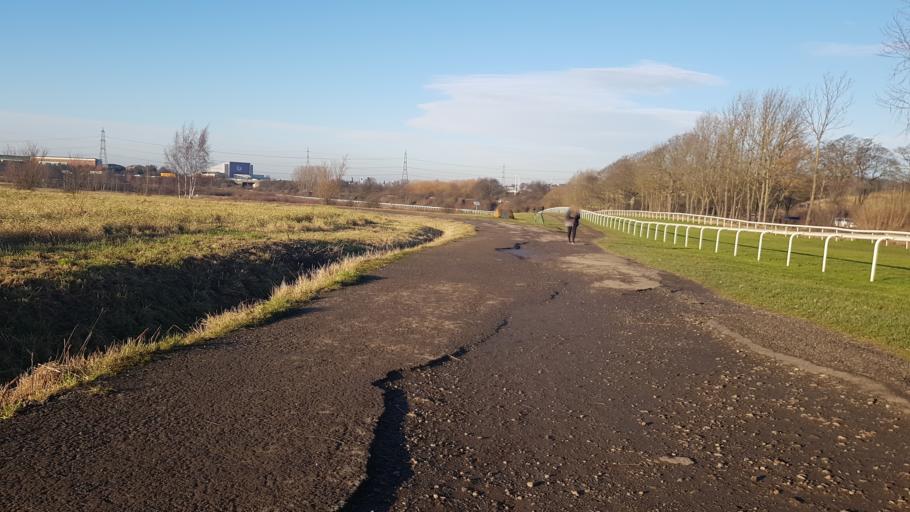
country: GB
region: England
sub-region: City and Borough of Wakefield
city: Pontefract
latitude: 53.7018
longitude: -1.3272
